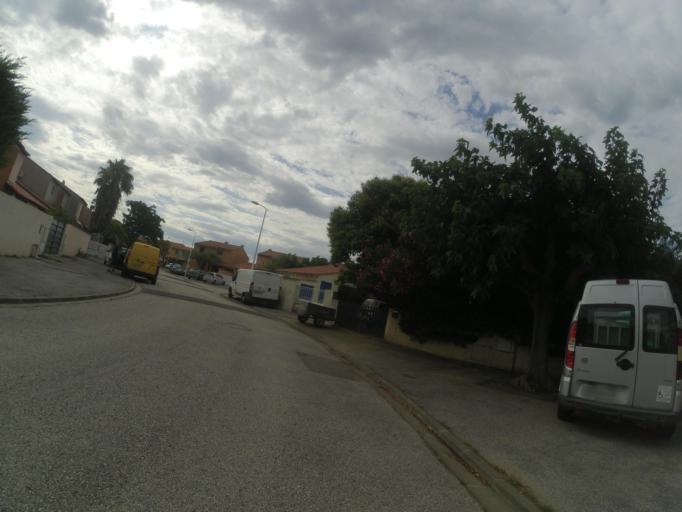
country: FR
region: Languedoc-Roussillon
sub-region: Departement des Pyrenees-Orientales
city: Toulouges
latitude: 42.6744
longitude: 2.8499
